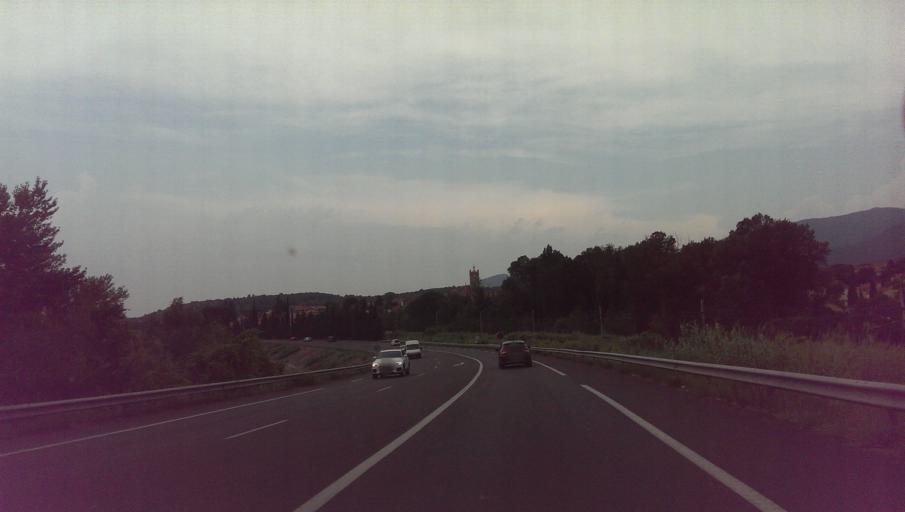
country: FR
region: Languedoc-Roussillon
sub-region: Departement des Pyrenees-Orientales
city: Vinca
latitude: 42.6466
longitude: 2.5206
